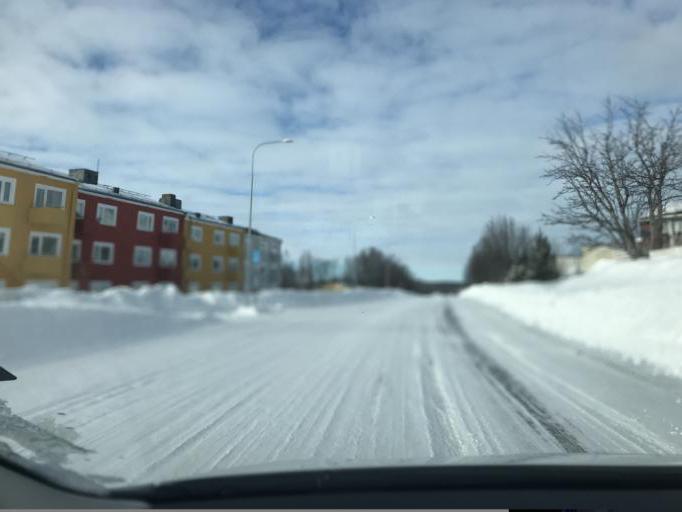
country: SE
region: Norrbotten
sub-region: Kiruna Kommun
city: Kiruna
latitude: 67.8638
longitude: 20.2096
